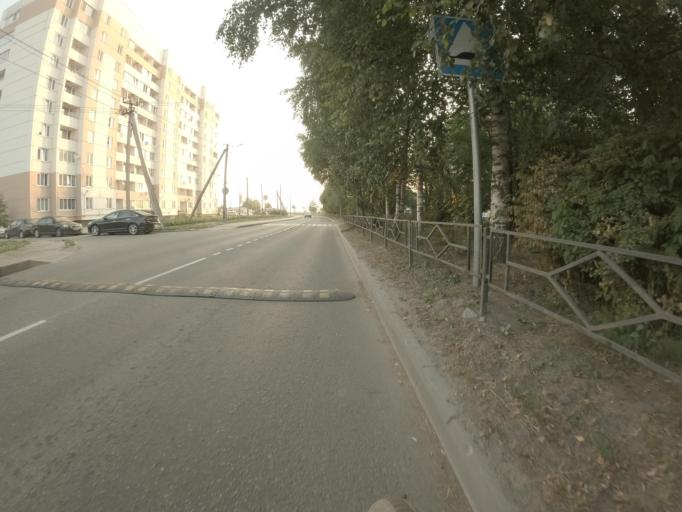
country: RU
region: St.-Petersburg
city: Pontonnyy
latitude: 59.7992
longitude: 30.6371
